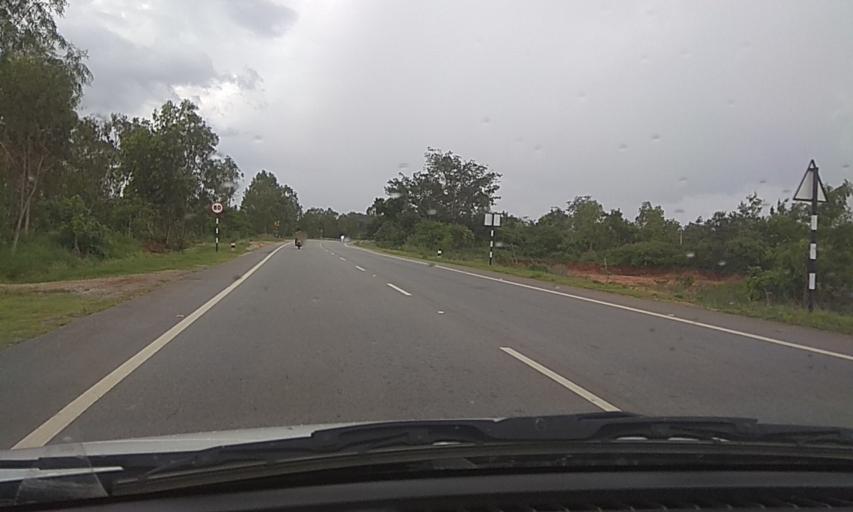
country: IN
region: Karnataka
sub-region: Mandya
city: Maddur
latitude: 12.7996
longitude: 77.0396
